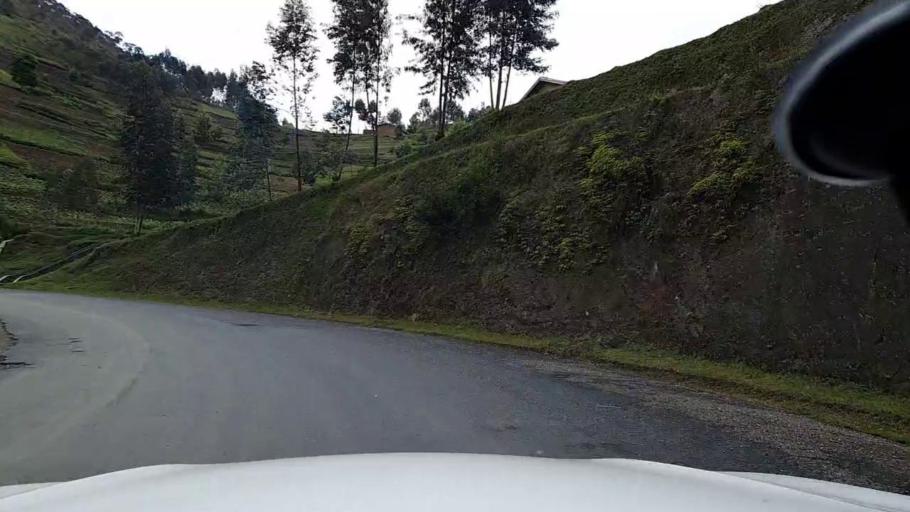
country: RW
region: Western Province
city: Kibuye
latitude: -2.0626
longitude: 29.5326
